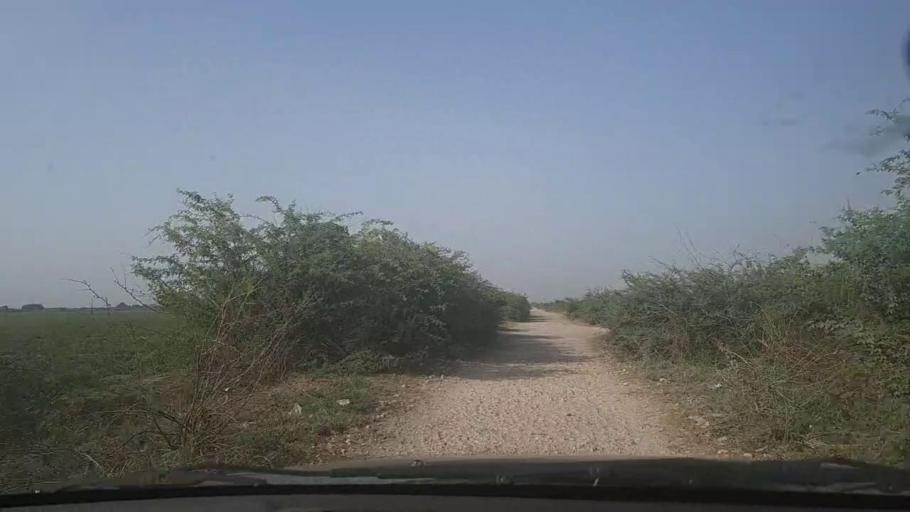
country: PK
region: Sindh
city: Keti Bandar
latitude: 24.2505
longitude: 67.5611
